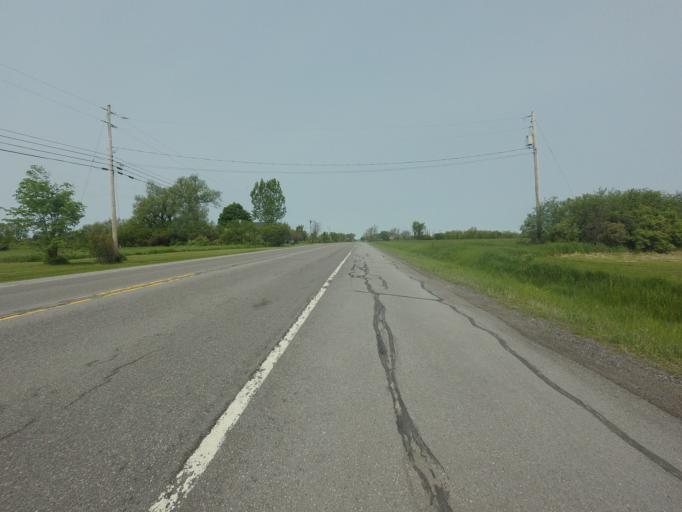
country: US
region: New York
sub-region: Jefferson County
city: Dexter
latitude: 44.0334
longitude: -76.0585
